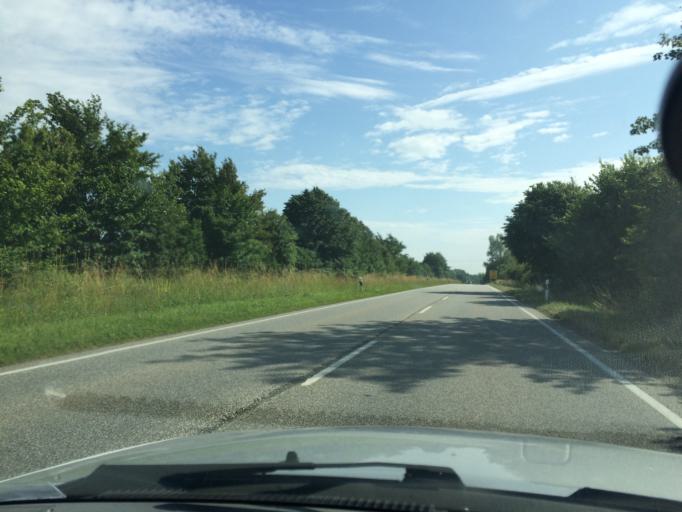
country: DE
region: Schleswig-Holstein
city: Oeversee
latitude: 54.7111
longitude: 9.4396
